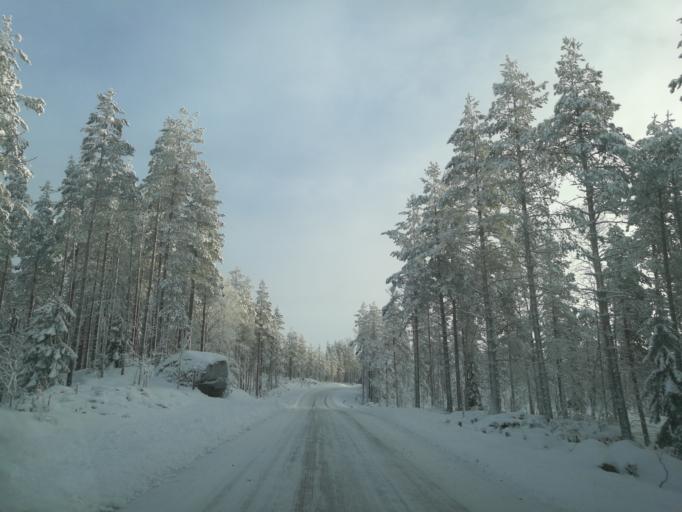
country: SE
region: Vaermland
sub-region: Torsby Kommun
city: Torsby
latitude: 60.6443
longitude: 12.7747
